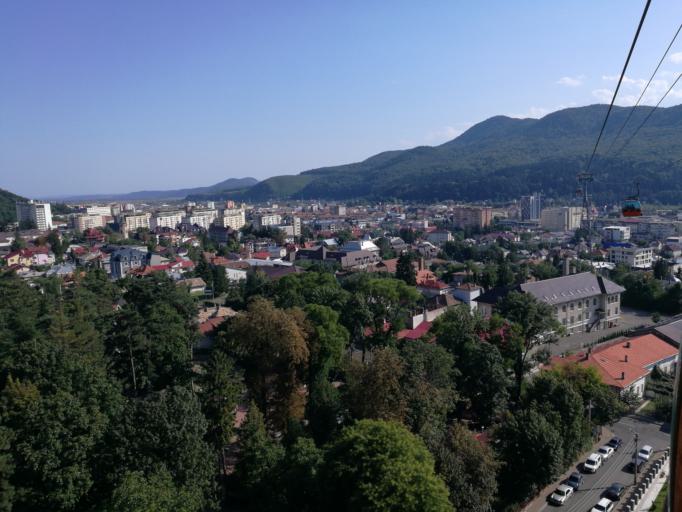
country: RO
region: Neamt
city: Piatra Neamt
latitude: 46.9371
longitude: 26.3647
